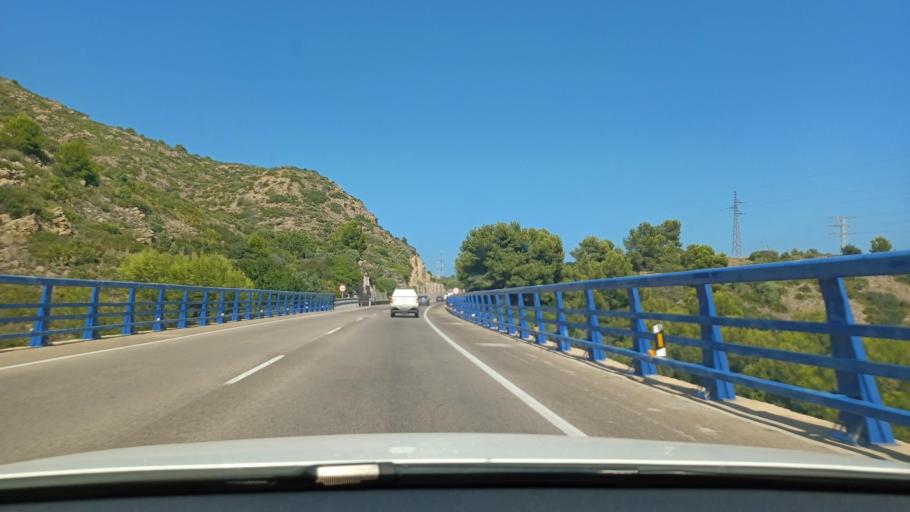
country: ES
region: Valencia
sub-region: Provincia de Castello
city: Benicassim
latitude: 40.0705
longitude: 0.1018
